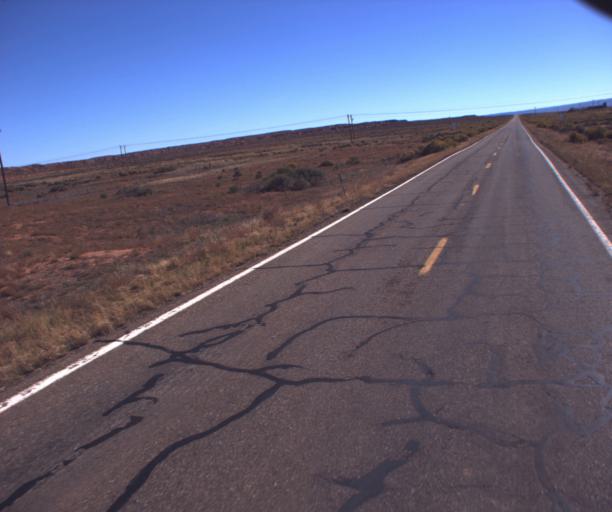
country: US
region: Arizona
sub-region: Coconino County
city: Fredonia
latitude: 36.9375
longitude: -112.5149
